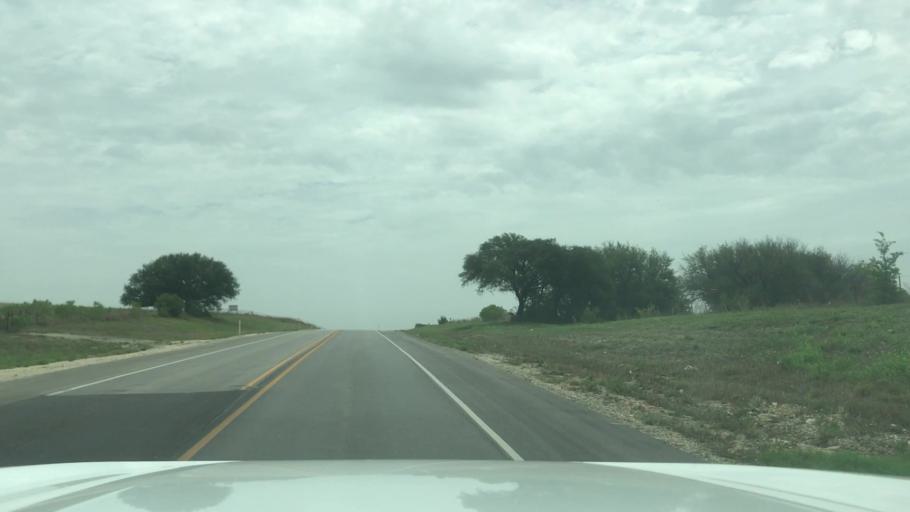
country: US
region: Texas
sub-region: Erath County
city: Dublin
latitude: 32.0734
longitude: -98.2267
